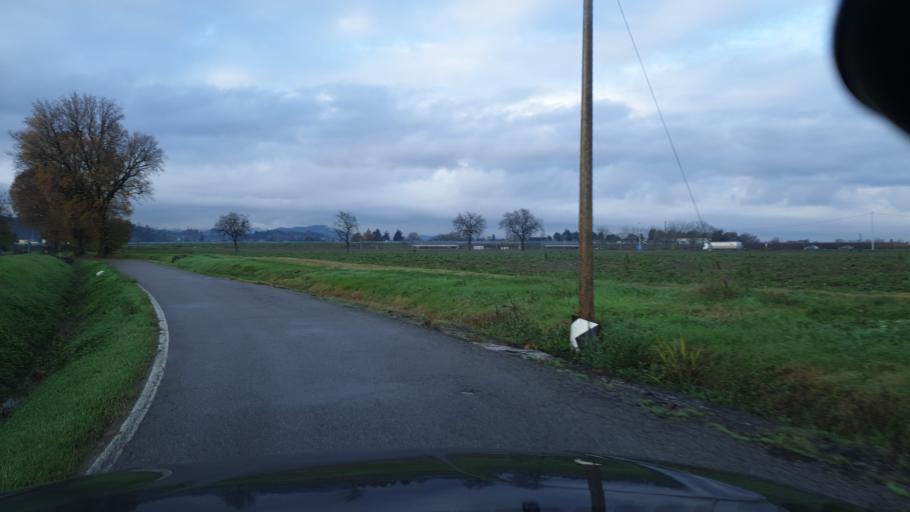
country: IT
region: Emilia-Romagna
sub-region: Provincia di Bologna
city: Crespellano
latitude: 44.5219
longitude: 11.1443
